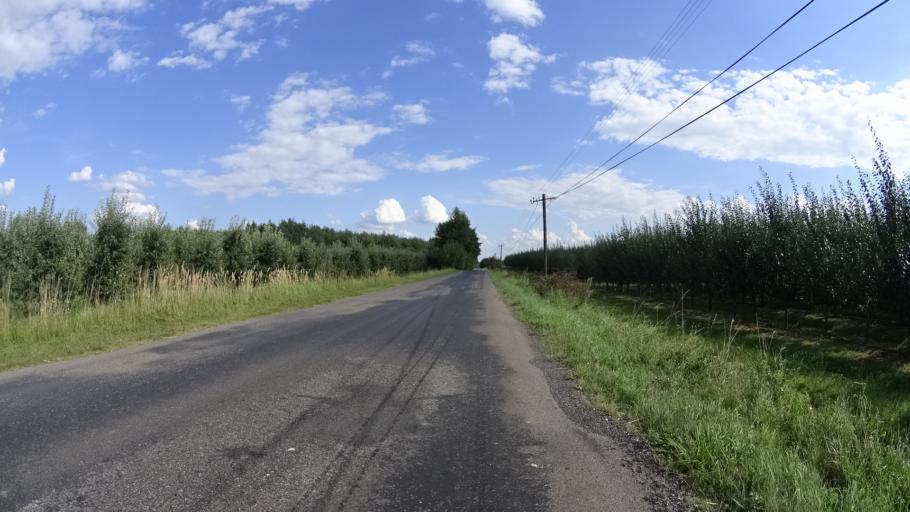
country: PL
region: Masovian Voivodeship
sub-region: Powiat grojecki
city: Mogielnica
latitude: 51.6880
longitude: 20.7517
